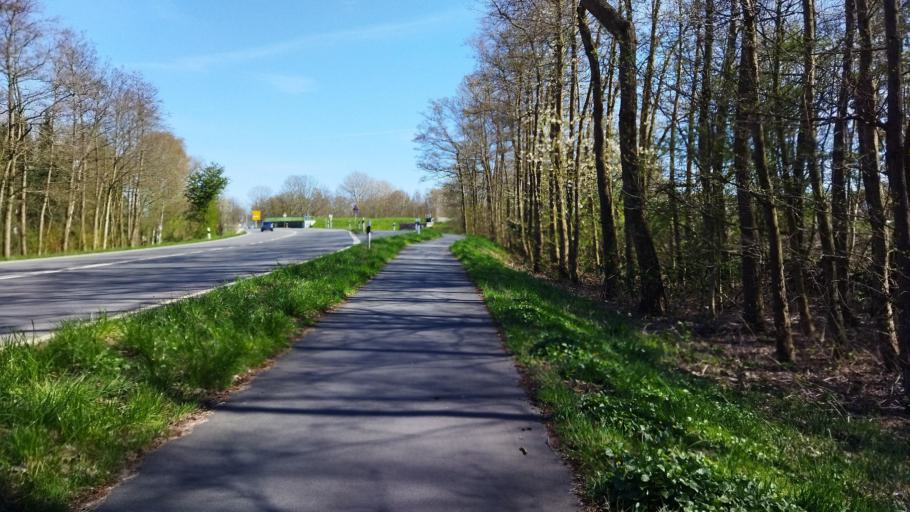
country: DE
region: Bremen
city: Bremerhaven
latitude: 53.5218
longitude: 8.5376
